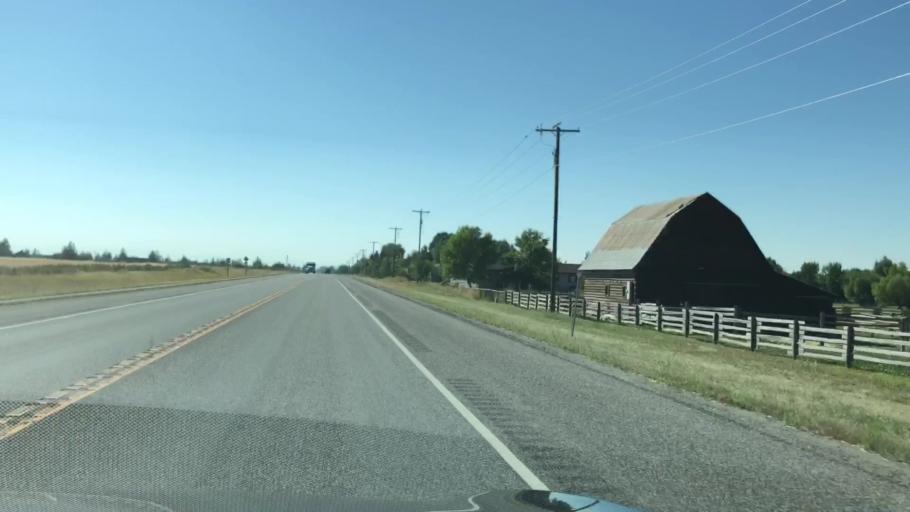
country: US
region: Montana
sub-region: Gallatin County
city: Belgrade
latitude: 45.7292
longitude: -111.1154
